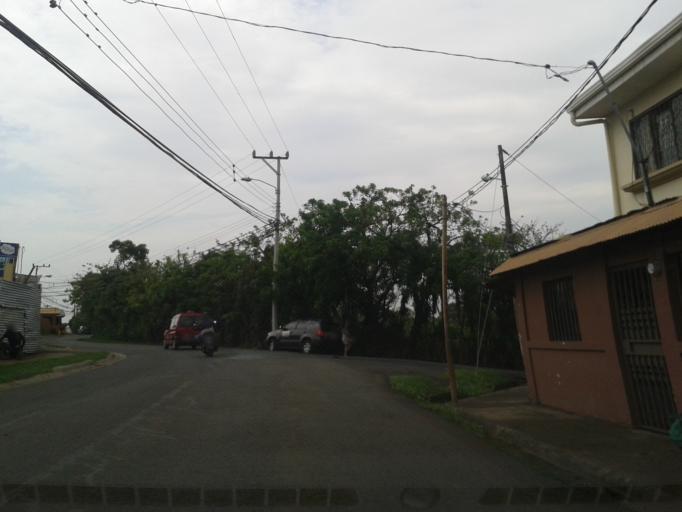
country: CR
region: Heredia
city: San Pablo
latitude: 9.9827
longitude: -84.1034
